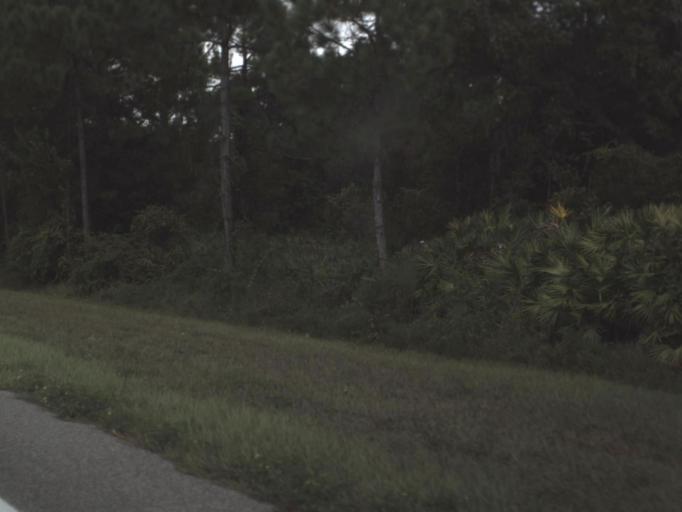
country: US
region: Florida
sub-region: Polk County
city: Frostproof
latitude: 27.7405
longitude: -81.5773
